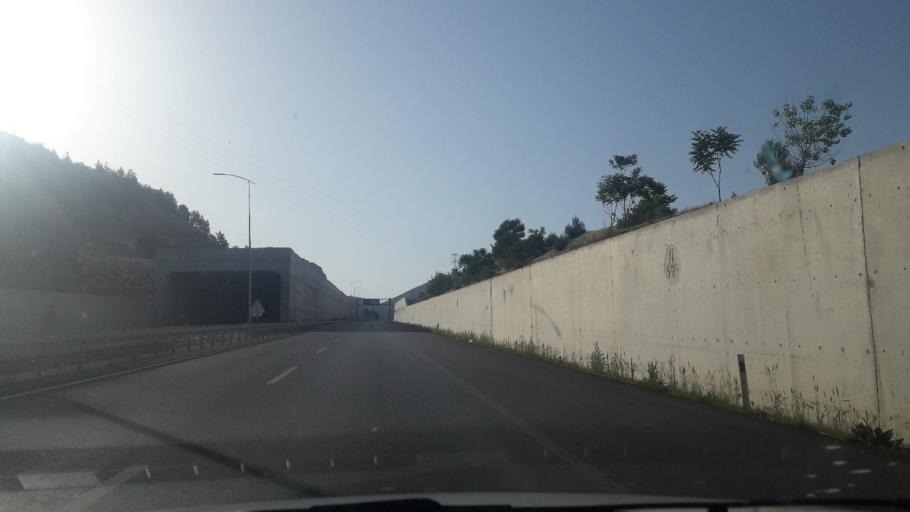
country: TR
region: Amasya
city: Amasya
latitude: 40.6420
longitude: 35.7952
